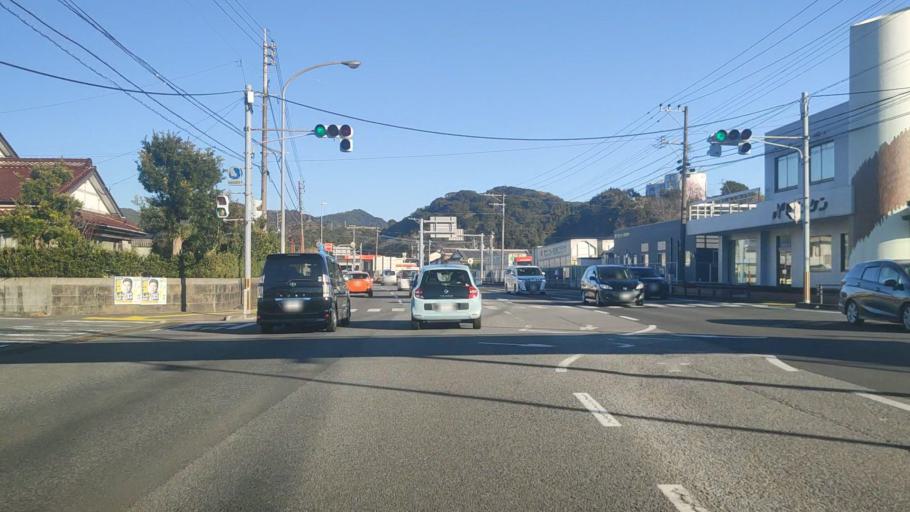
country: JP
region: Miyazaki
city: Nobeoka
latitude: 32.4881
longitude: 131.6643
